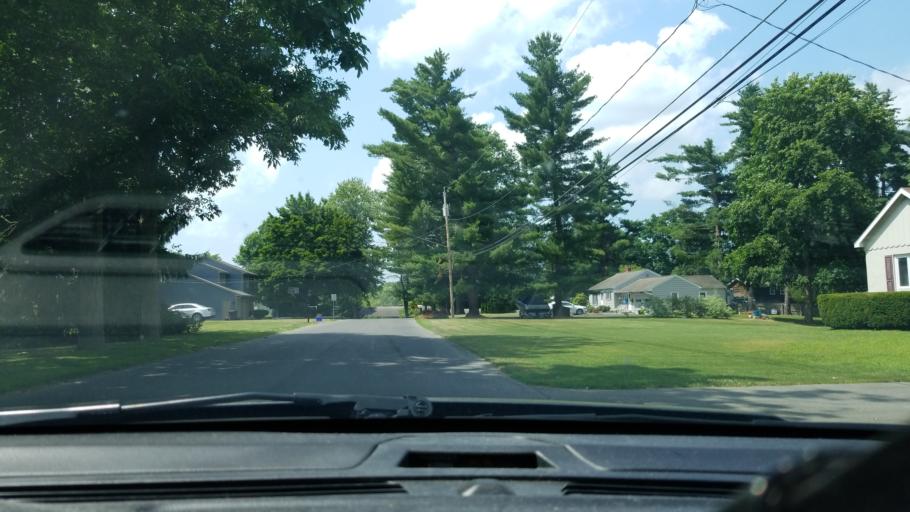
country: US
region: New York
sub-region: Onondaga County
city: Liverpool
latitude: 43.1368
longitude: -76.2354
